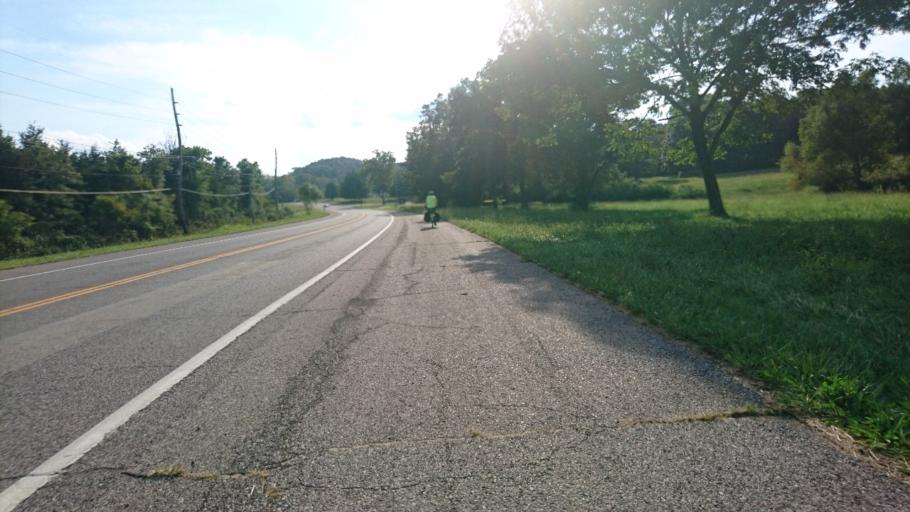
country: US
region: Missouri
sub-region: Saint Louis County
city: Eureka
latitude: 38.5034
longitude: -90.6846
